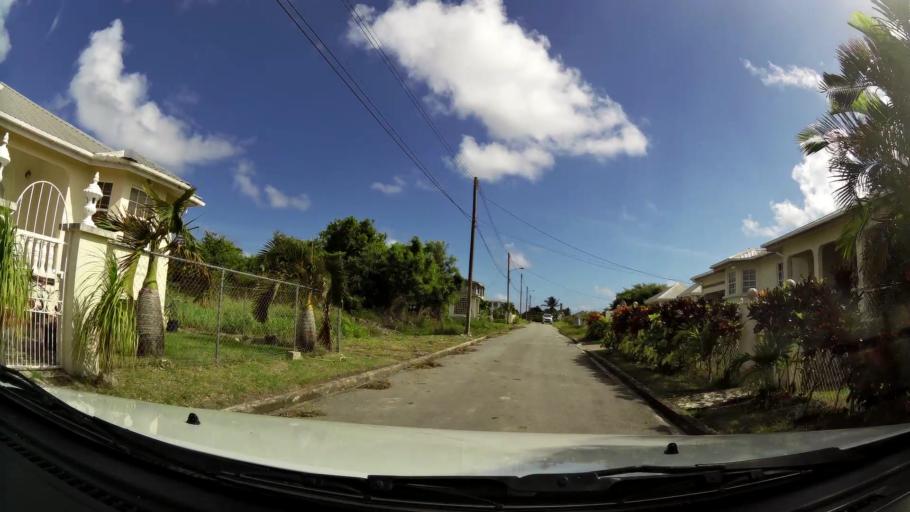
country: BB
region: Saint Lucy
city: Checker Hall
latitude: 13.2957
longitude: -59.6471
